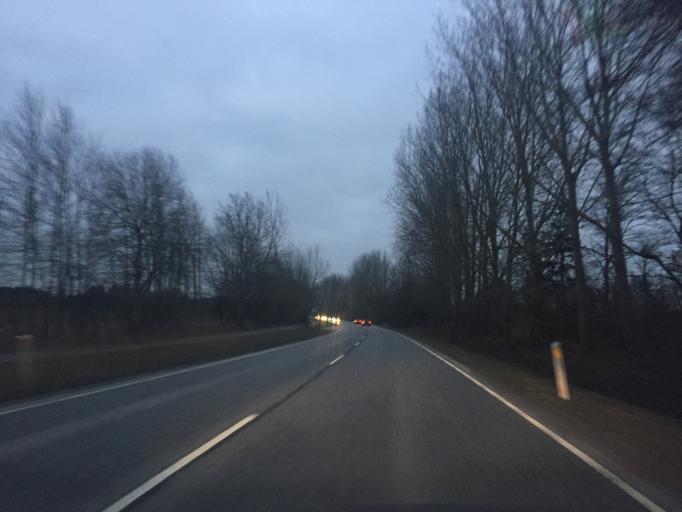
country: DK
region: Capital Region
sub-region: Frederikssund Kommune
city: Slangerup
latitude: 55.8399
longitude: 12.1596
